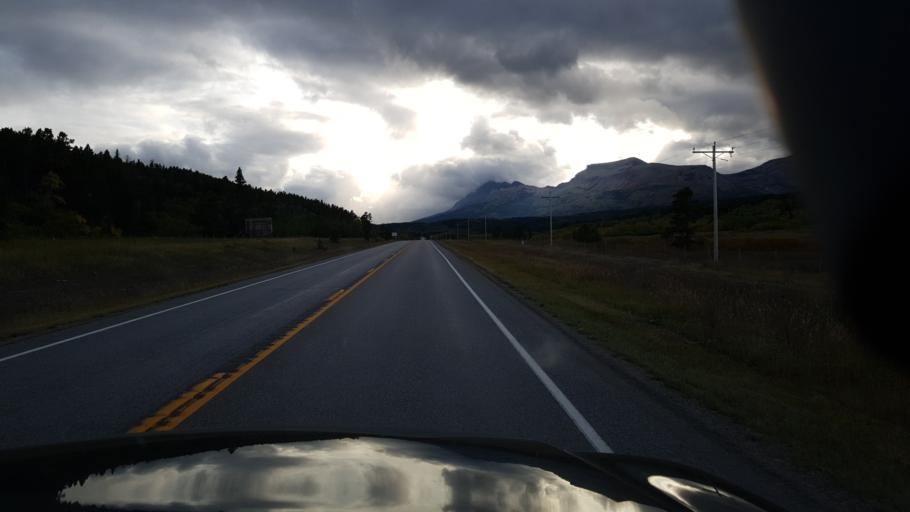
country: US
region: Montana
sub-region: Glacier County
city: South Browning
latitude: 48.4168
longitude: -113.2218
